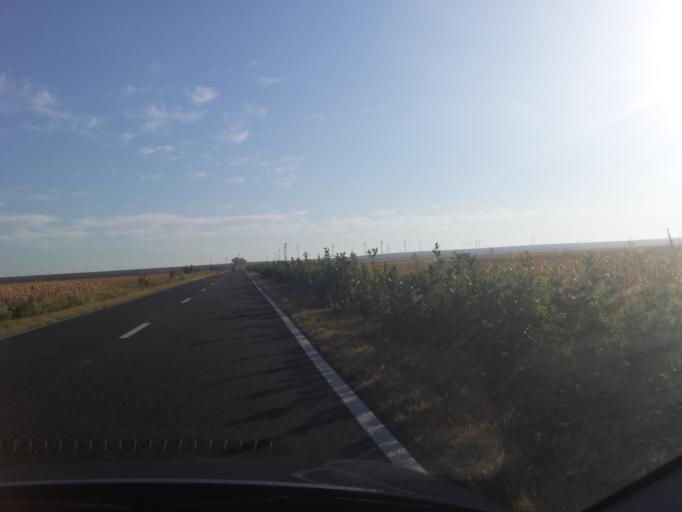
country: RO
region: Constanta
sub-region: Comuna Saraiu
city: Saraiu
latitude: 44.7483
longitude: 28.1864
